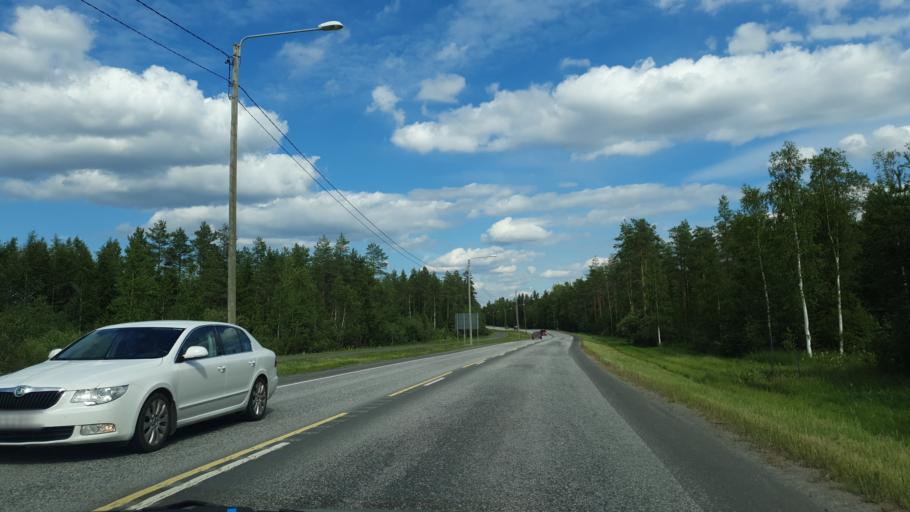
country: FI
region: Kainuu
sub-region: Kajaani
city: Kajaani
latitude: 64.2589
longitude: 27.8263
